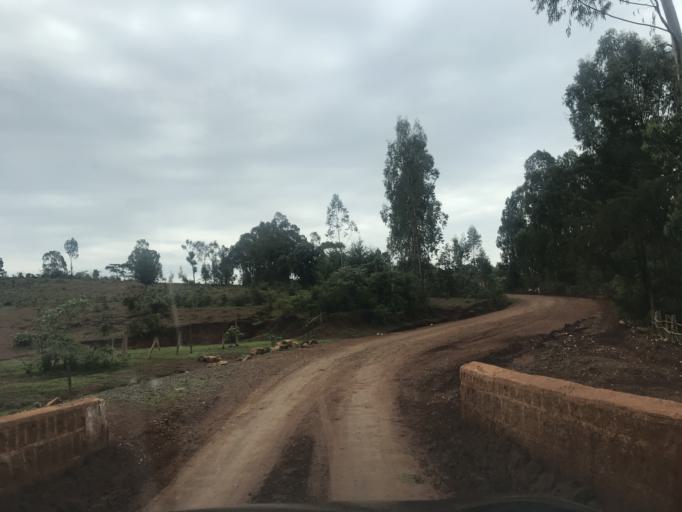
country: ET
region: Oromiya
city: Shambu
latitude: 9.8847
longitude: 36.6513
